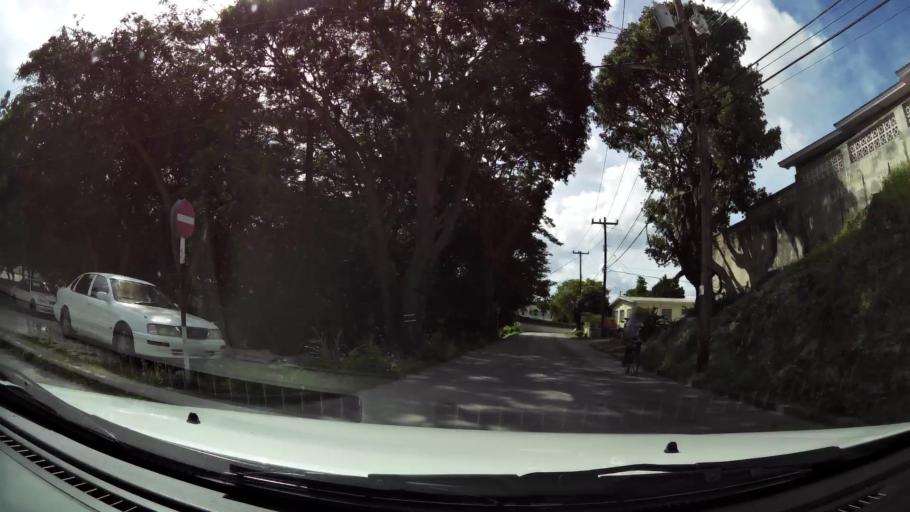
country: BB
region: Saint Michael
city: Bridgetown
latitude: 13.1001
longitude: -59.5943
